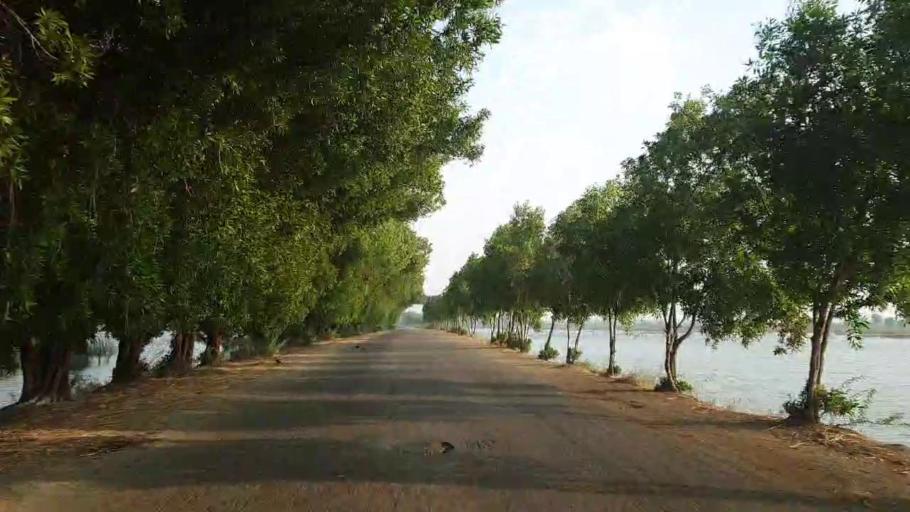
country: PK
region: Sindh
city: Tando Bago
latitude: 24.7475
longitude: 68.9490
